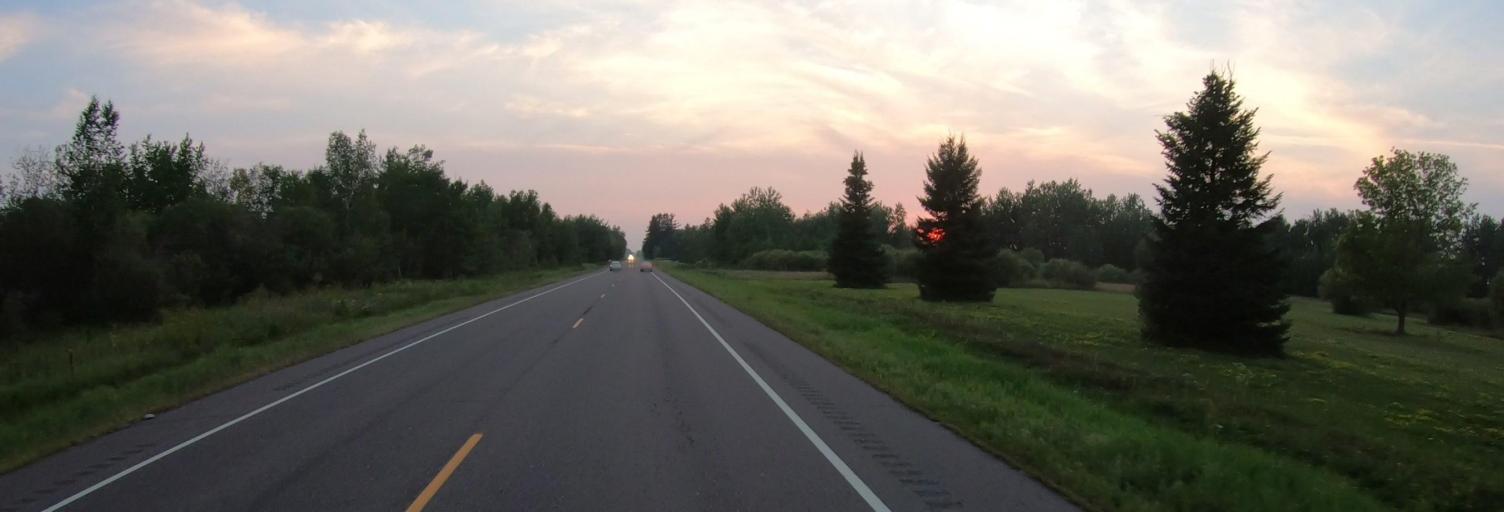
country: US
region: Minnesota
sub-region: Pine County
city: Rock Creek
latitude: 45.7735
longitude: -92.8758
